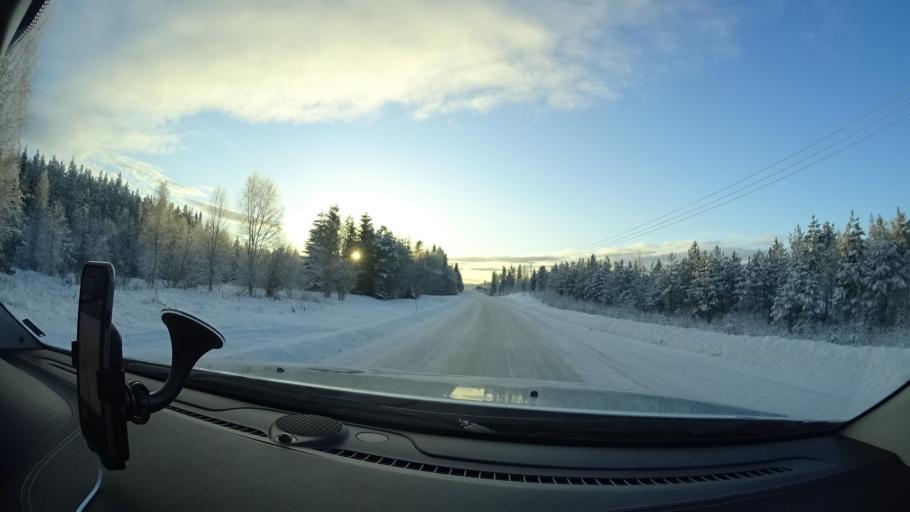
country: SE
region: Jaemtland
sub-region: Ragunda Kommun
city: Hammarstrand
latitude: 63.2047
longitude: 15.9463
